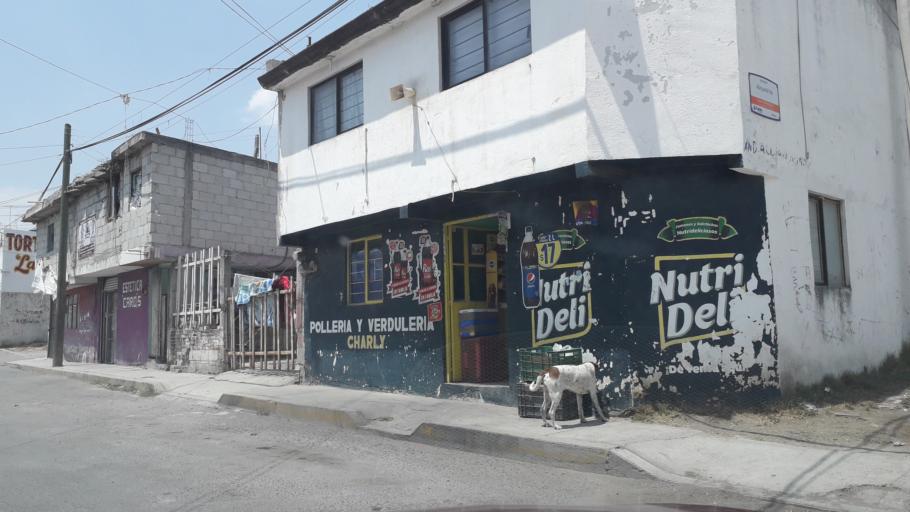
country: MX
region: Puebla
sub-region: Puebla
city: Galaxia la Calera
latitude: 18.9948
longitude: -98.1819
